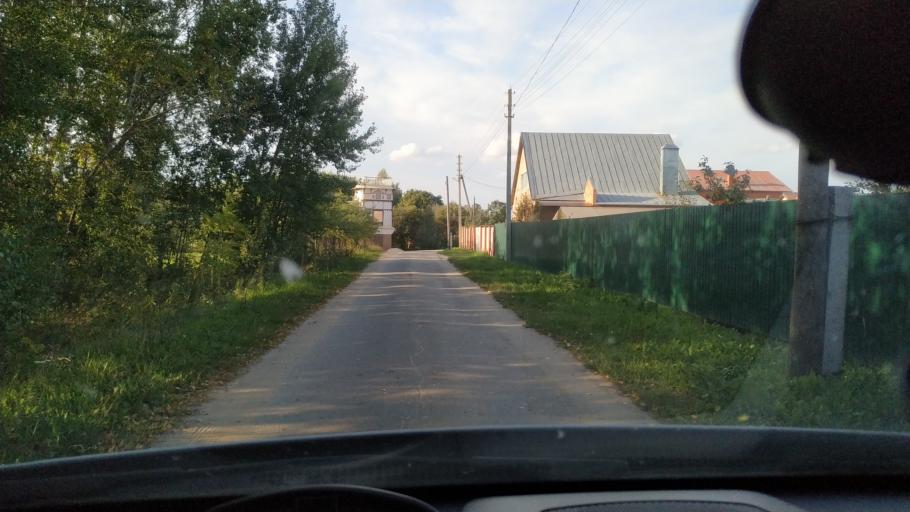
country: RU
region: Rjazan
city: Solotcha
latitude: 54.8669
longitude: 39.6697
